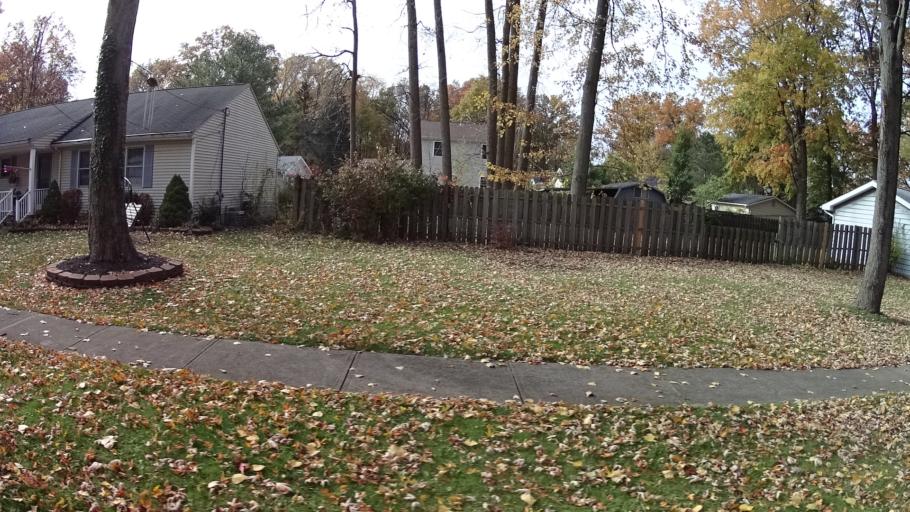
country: US
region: Ohio
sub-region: Lorain County
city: Sheffield Lake
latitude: 41.4834
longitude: -82.0967
